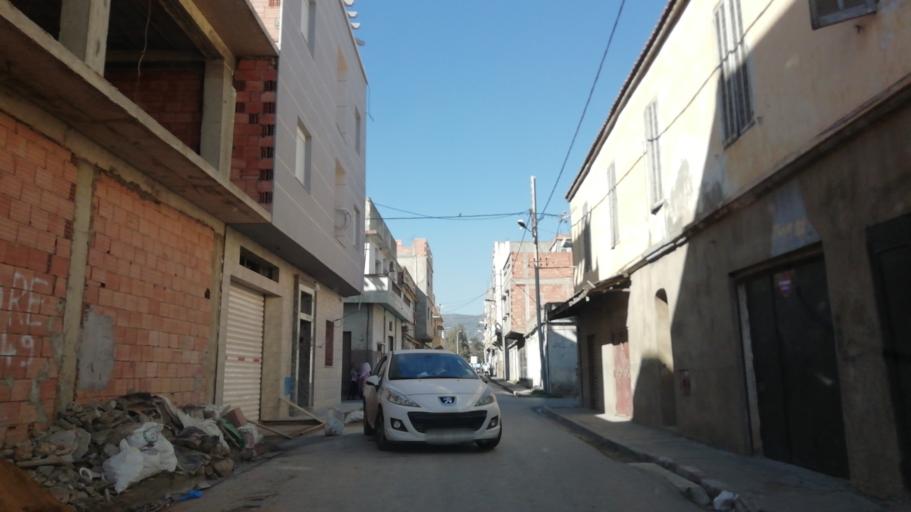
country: DZ
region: Oran
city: Oran
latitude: 35.6900
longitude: -0.6397
